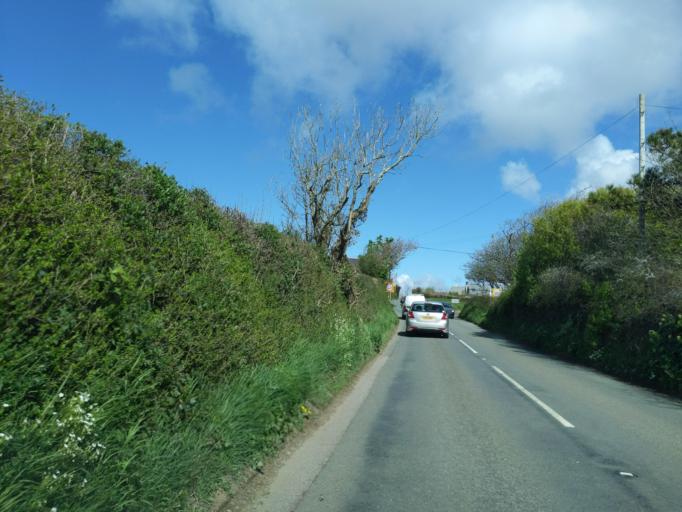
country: GB
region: England
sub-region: Cornwall
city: Wadebridge
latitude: 50.5794
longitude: -4.7962
